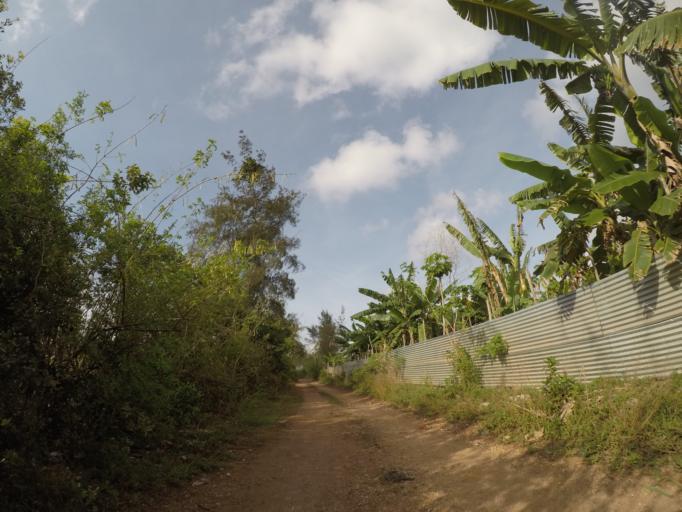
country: TZ
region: Zanzibar Central/South
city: Koani
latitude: -6.2217
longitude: 39.3194
